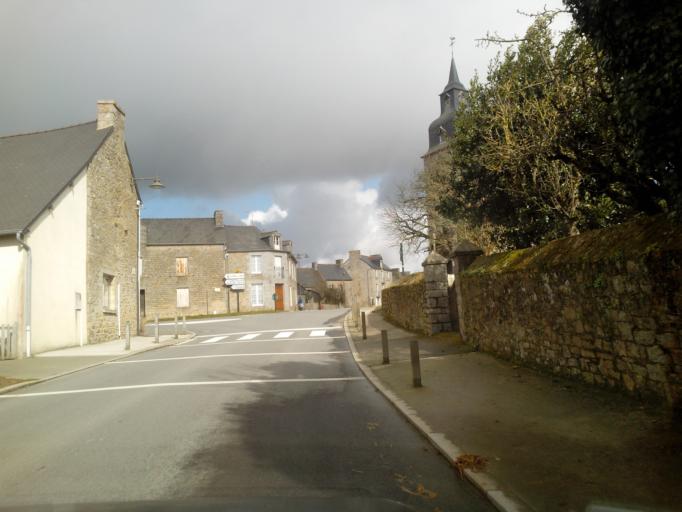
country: FR
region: Brittany
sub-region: Departement des Cotes-d'Armor
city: Broons
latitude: 48.3743
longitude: -2.2502
